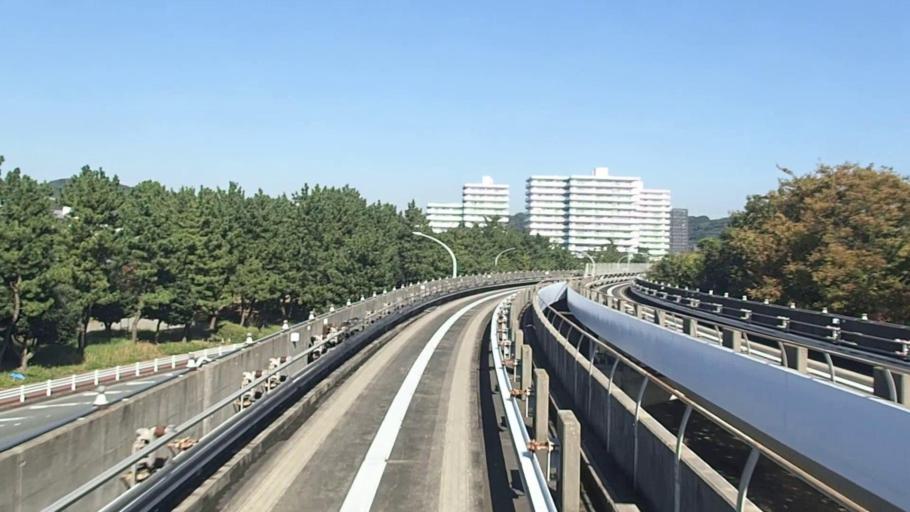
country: JP
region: Kanagawa
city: Yokosuka
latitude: 35.3376
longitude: 139.6321
